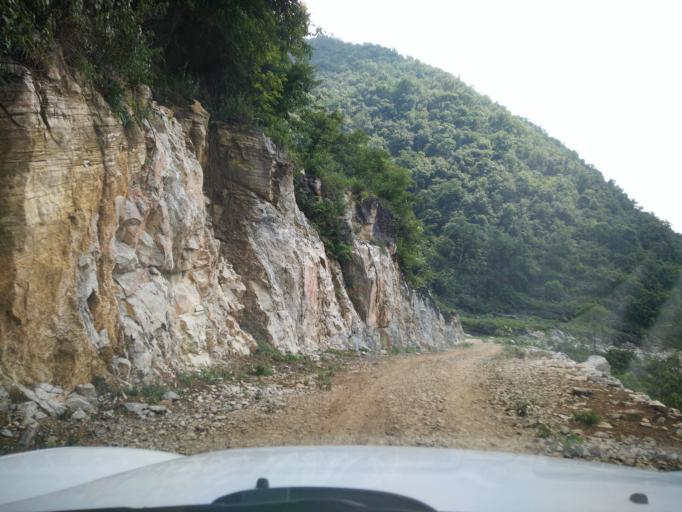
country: CN
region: Guangxi Zhuangzu Zizhiqu
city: Xinzhou
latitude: 25.1351
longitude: 105.6737
